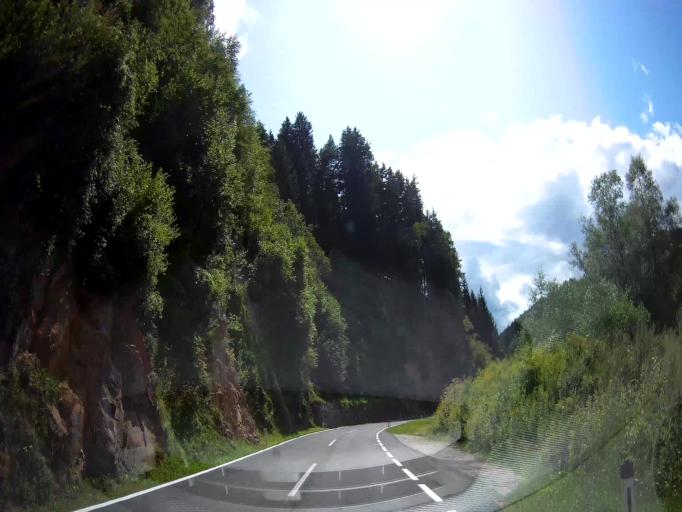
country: AT
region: Carinthia
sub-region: Politischer Bezirk Spittal an der Drau
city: Seeboden
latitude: 46.8472
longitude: 13.5034
